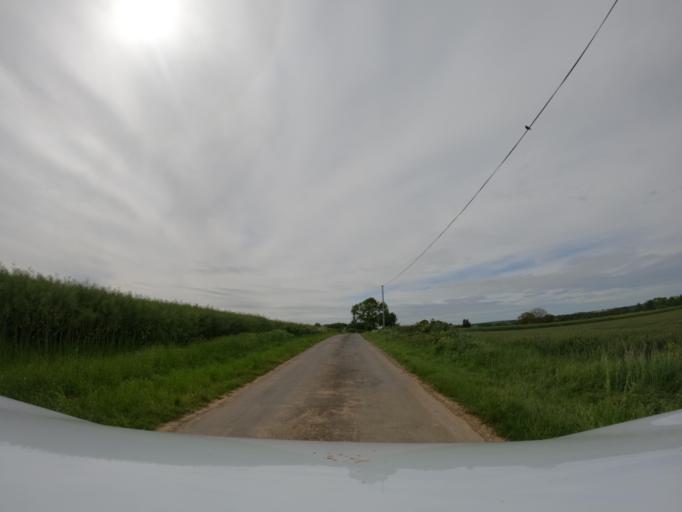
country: FR
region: Pays de la Loire
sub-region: Departement de la Vendee
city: Saint-Hilaire-des-Loges
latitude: 46.5002
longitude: -0.6355
